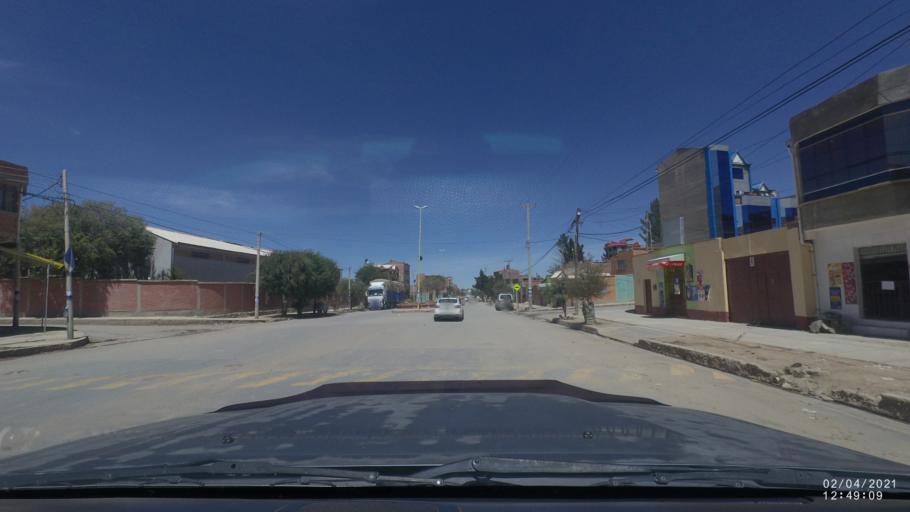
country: BO
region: Oruro
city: Oruro
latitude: -17.9708
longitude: -67.1388
